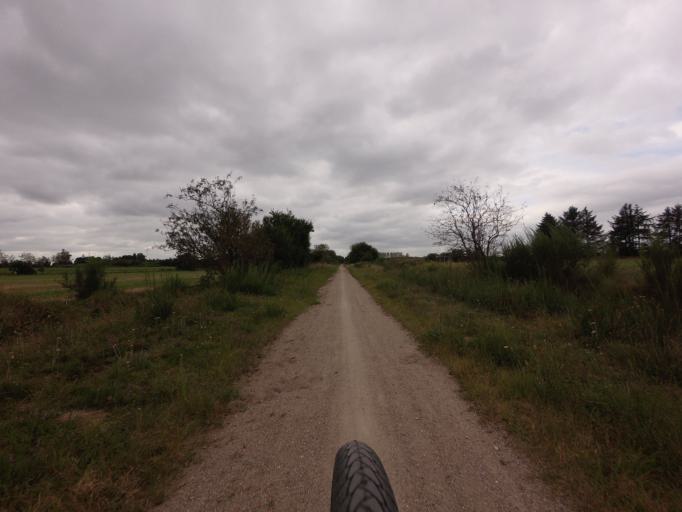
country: DK
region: South Denmark
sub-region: Billund Kommune
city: Grindsted
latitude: 55.7902
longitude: 8.9692
